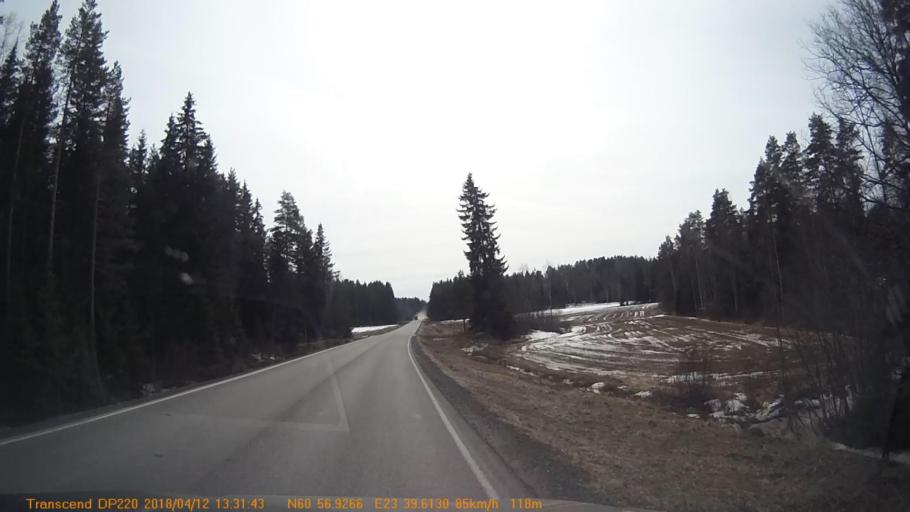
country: FI
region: Haeme
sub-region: Forssa
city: Forssa
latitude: 60.9487
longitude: 23.6602
